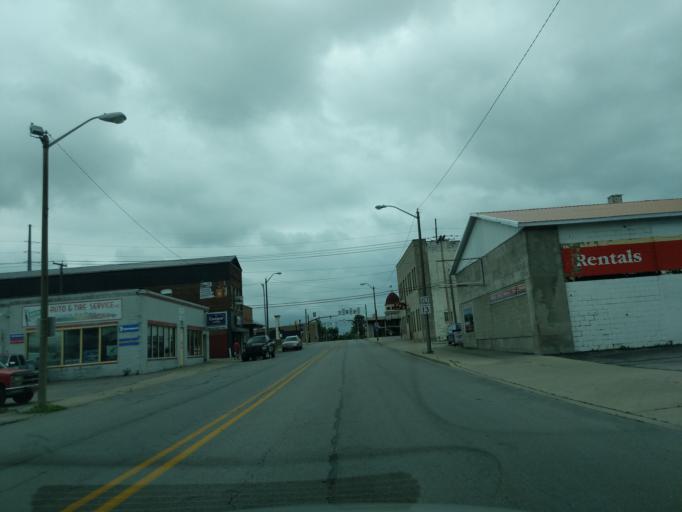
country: US
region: Indiana
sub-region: Madison County
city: Elwood
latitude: 40.2769
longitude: -85.8437
